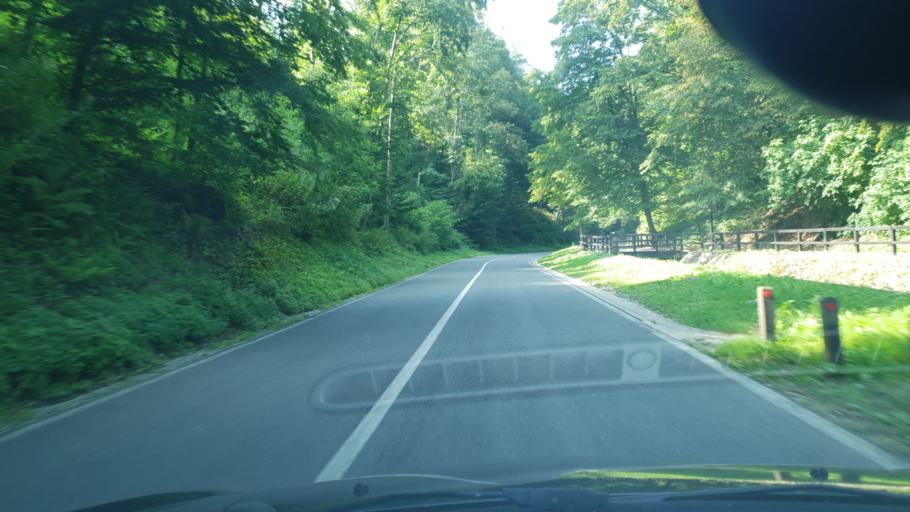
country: HR
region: Grad Zagreb
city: Kasina
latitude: 45.8718
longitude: 15.9784
